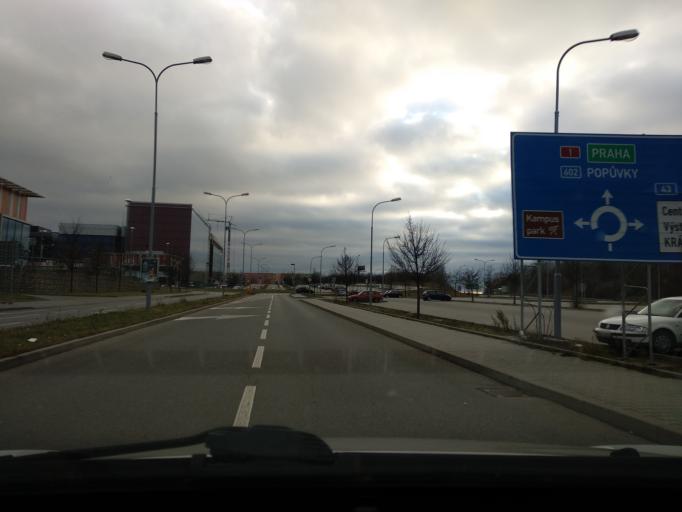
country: CZ
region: South Moravian
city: Ostopovice
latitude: 49.1779
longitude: 16.5647
